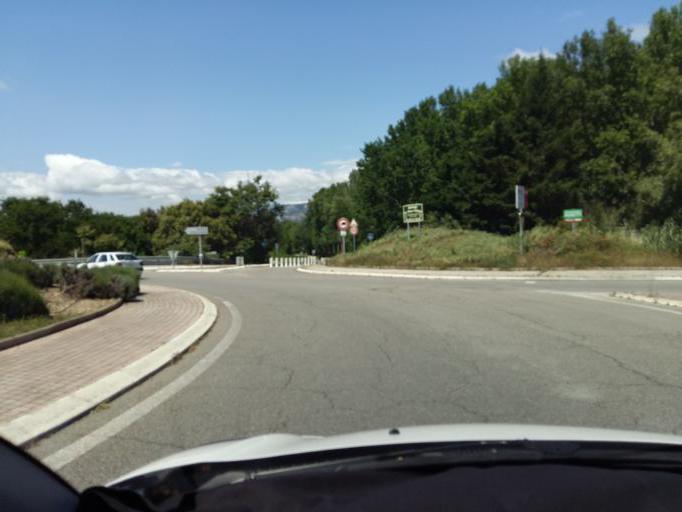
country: FR
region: Provence-Alpes-Cote d'Azur
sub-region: Departement des Bouches-du-Rhone
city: Mallemort
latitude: 43.7104
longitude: 5.1952
